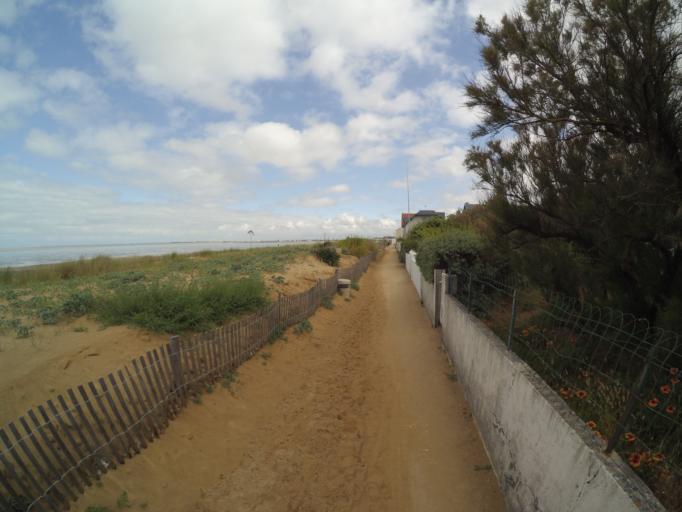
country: FR
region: Poitou-Charentes
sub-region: Departement de la Charente-Maritime
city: Chatelaillon-Plage
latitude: 46.0672
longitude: -1.0929
